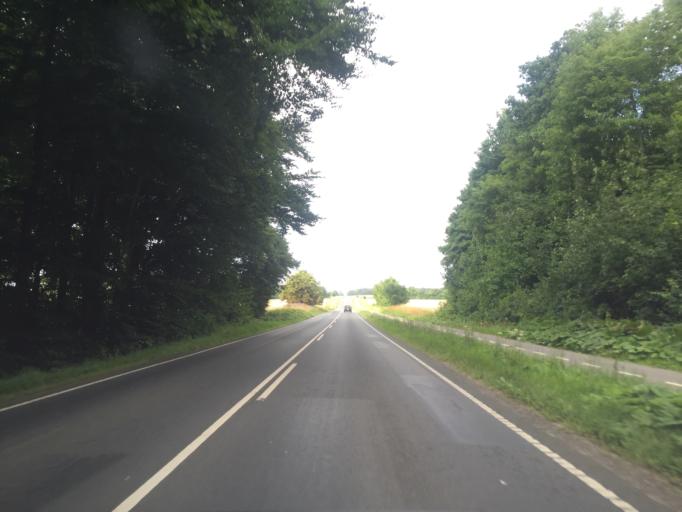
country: DK
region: South Denmark
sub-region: Svendborg Kommune
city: Thuro By
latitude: 55.0815
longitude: 10.6722
